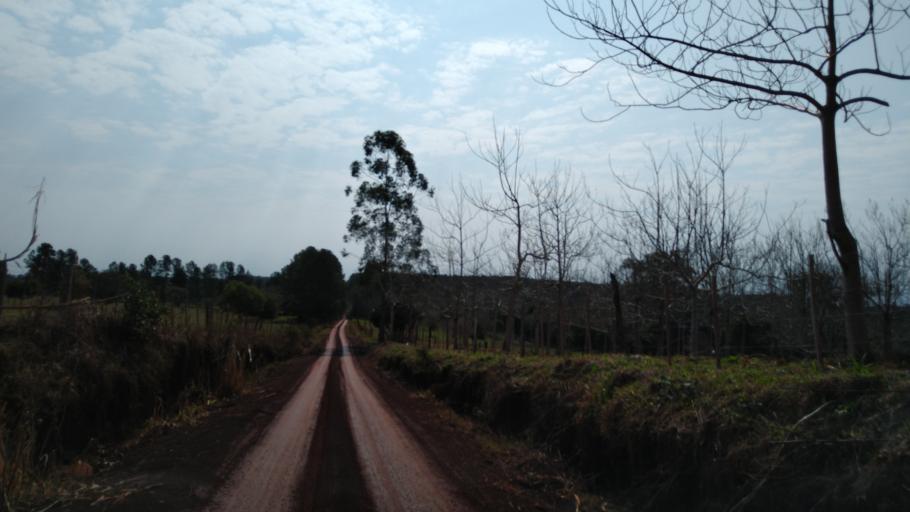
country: AR
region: Misiones
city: Capiovi
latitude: -26.9513
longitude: -55.0444
